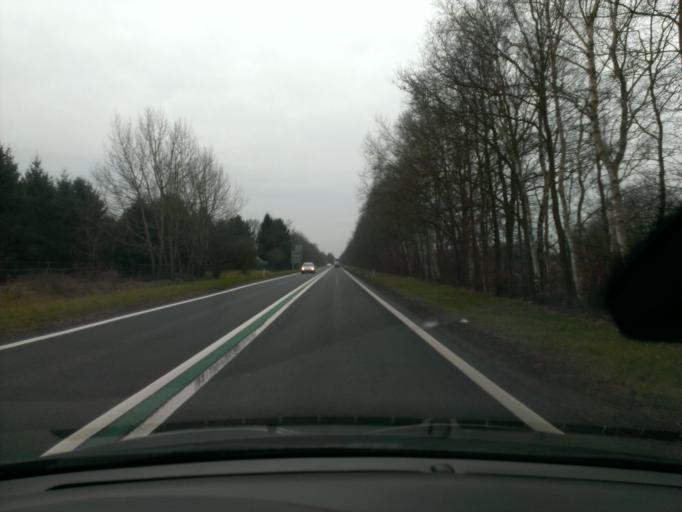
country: NL
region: Overijssel
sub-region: Gemeente Twenterand
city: Westerhaar-Vriezenveensewijk
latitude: 52.4617
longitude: 6.6261
